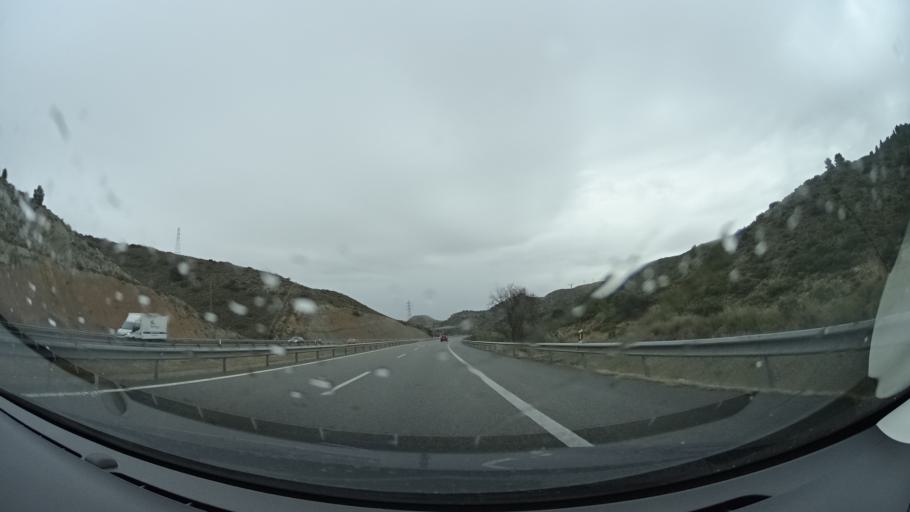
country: ES
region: Aragon
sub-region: Provincia de Huesca
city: Fraga
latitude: 41.4657
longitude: 0.2946
